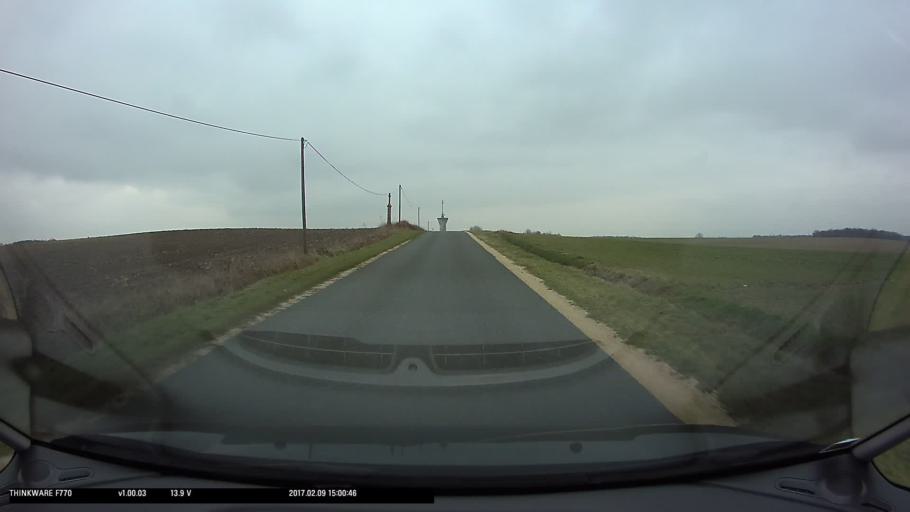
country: FR
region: Centre
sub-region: Departement du Cher
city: Orval
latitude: 46.8181
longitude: 2.4387
